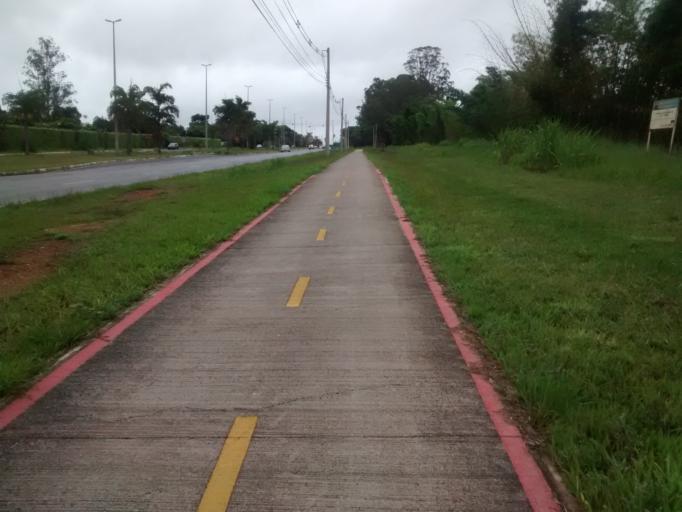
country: BR
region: Federal District
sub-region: Brasilia
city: Brasilia
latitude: -15.7775
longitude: -47.8713
